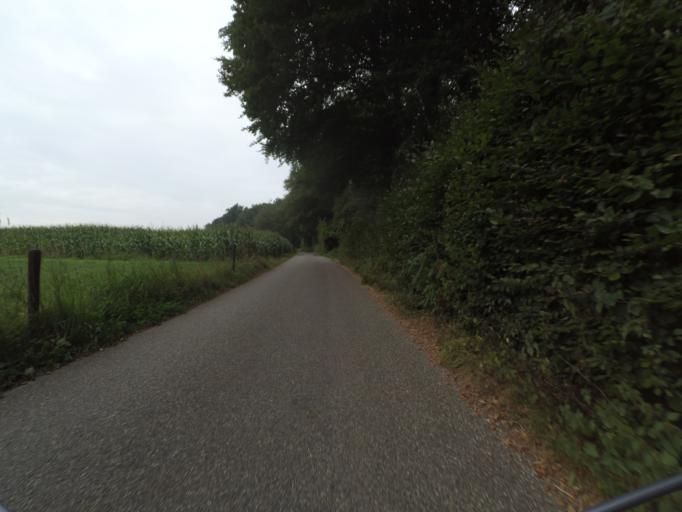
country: NL
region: Overijssel
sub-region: Gemeente Oldenzaal
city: Oldenzaal
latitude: 52.3179
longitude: 6.9667
